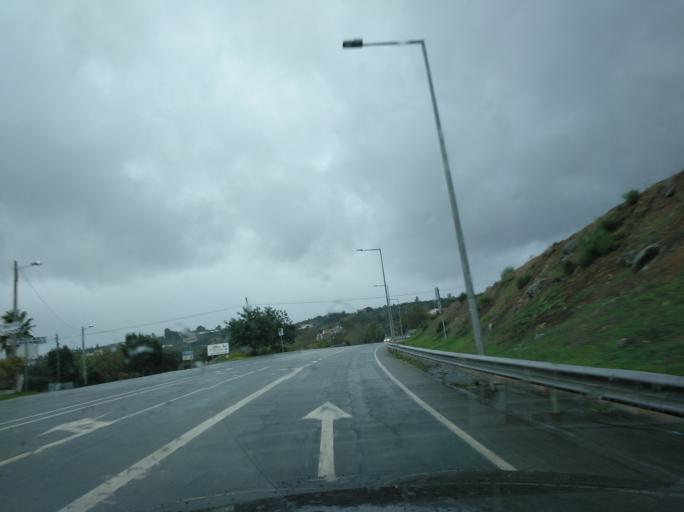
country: PT
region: Portalegre
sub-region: Elvas
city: Elvas
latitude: 38.8701
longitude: -7.2015
